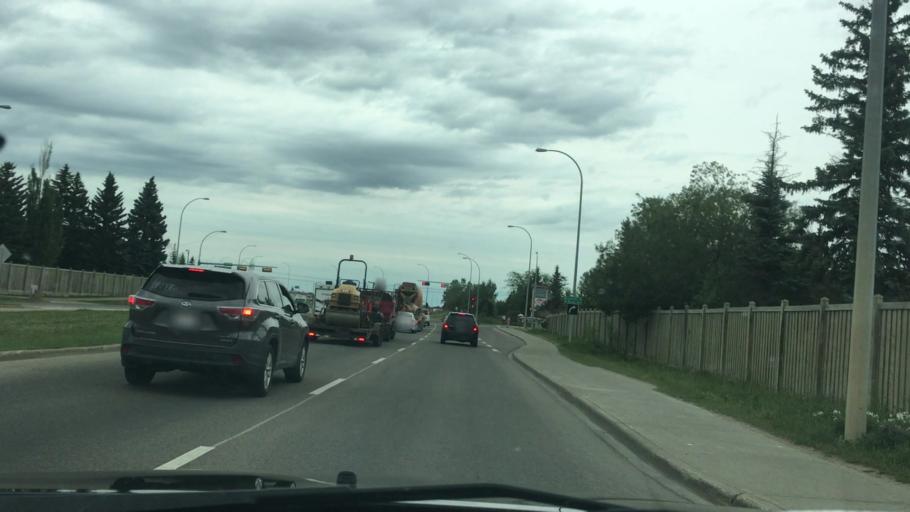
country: CA
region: Alberta
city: Beaumont
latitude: 53.4282
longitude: -113.5164
